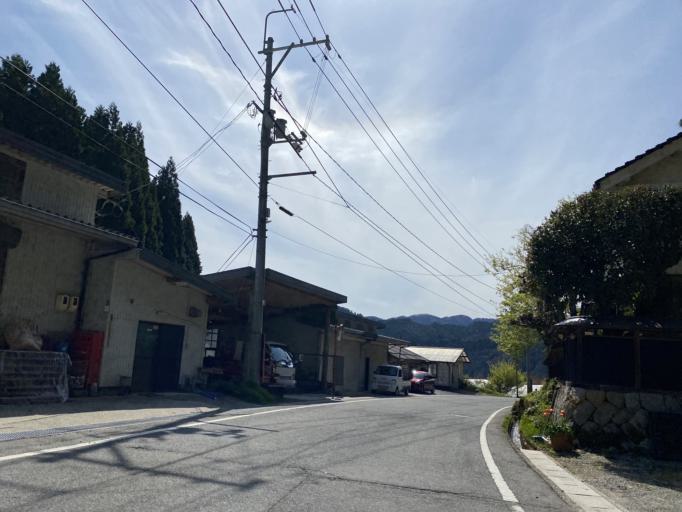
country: JP
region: Hyogo
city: Yamazakicho-nakabirose
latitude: 35.1661
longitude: 134.3418
